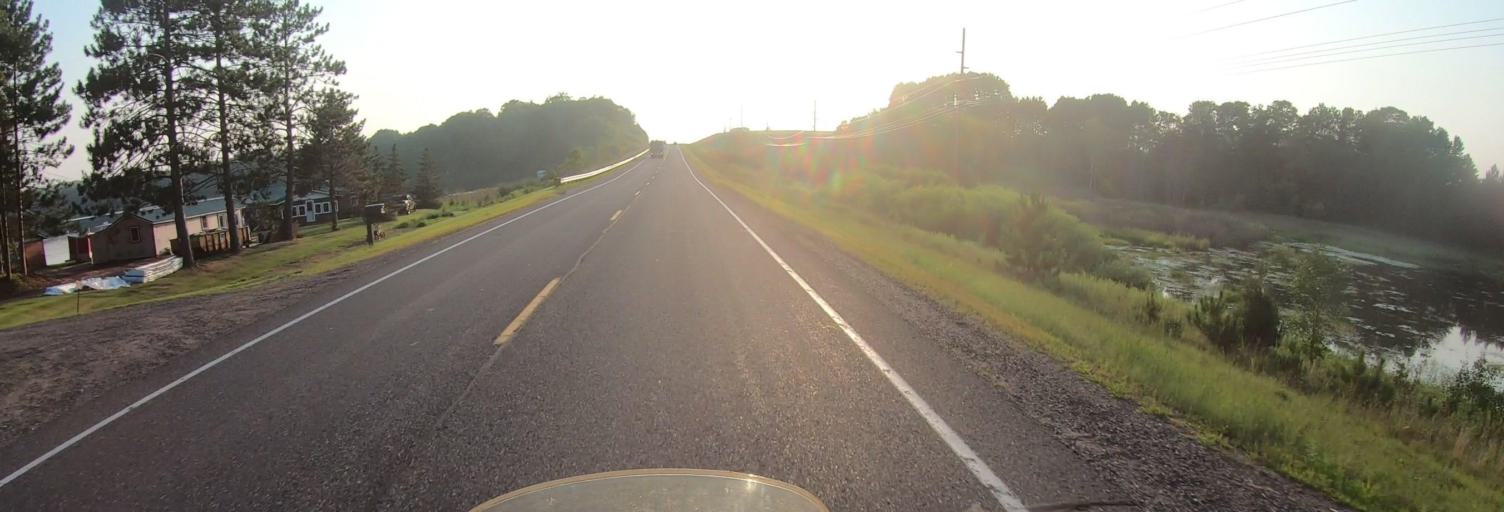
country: US
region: Wisconsin
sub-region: Washburn County
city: Shell Lake
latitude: 45.8154
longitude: -92.0652
